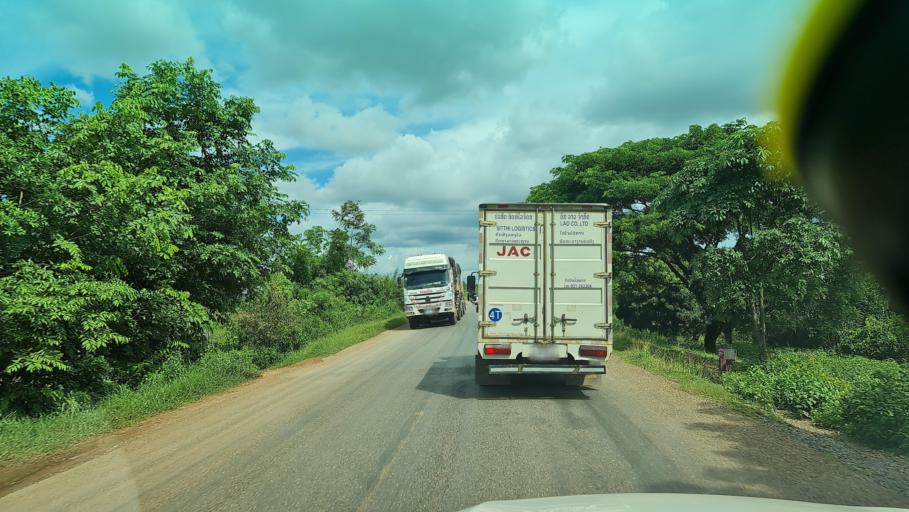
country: LA
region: Bolikhamxai
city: Ban Nahin
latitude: 18.1882
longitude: 104.2242
